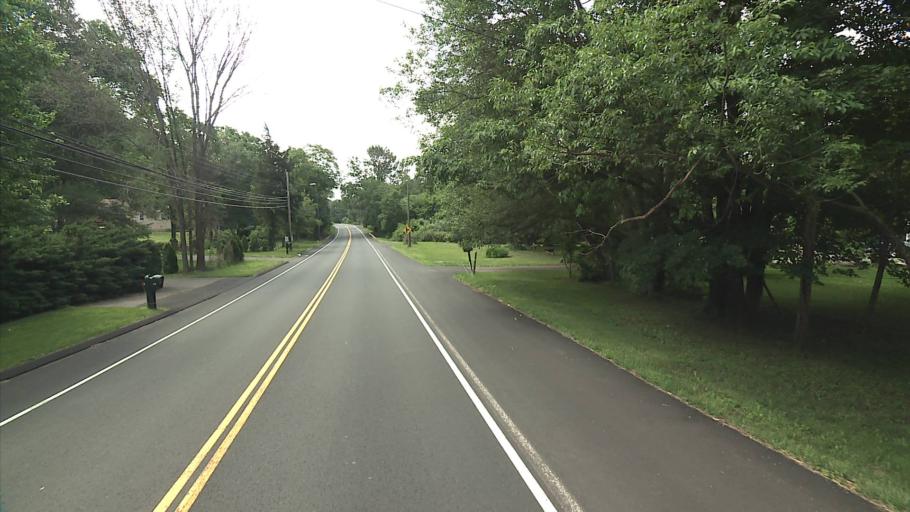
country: US
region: Connecticut
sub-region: New Haven County
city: North Branford
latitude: 41.3480
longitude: -72.8014
